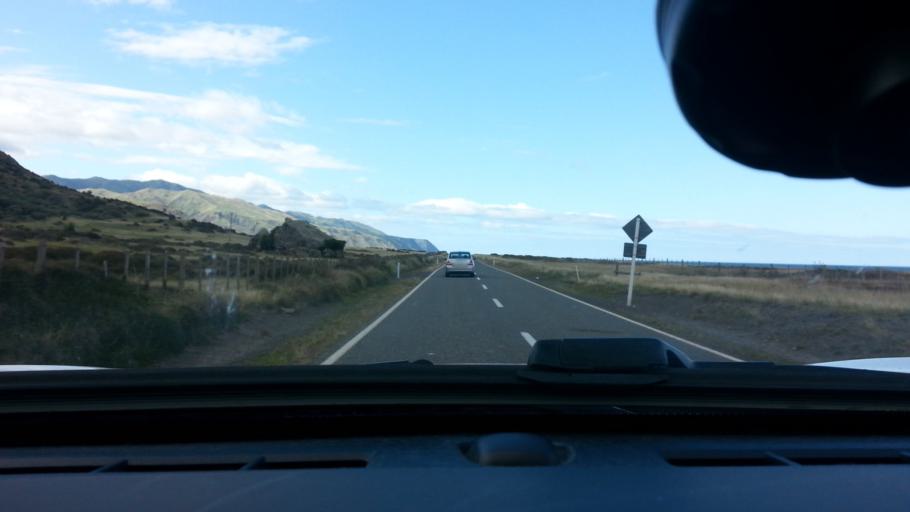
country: NZ
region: Wellington
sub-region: South Wairarapa District
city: Waipawa
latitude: -41.5219
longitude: 175.1980
